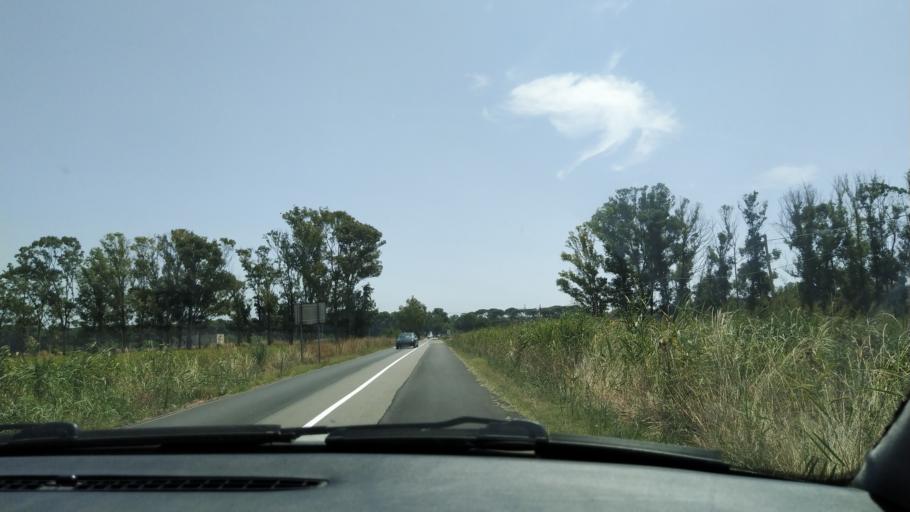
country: IT
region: Basilicate
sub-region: Provincia di Matera
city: Marconia
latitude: 40.3262
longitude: 16.7897
